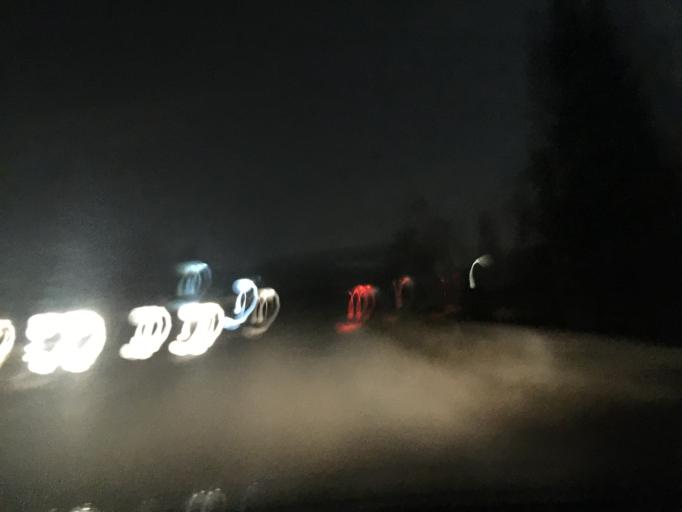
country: JO
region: Amman
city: Umm as Summaq
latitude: 31.8868
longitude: 35.8439
